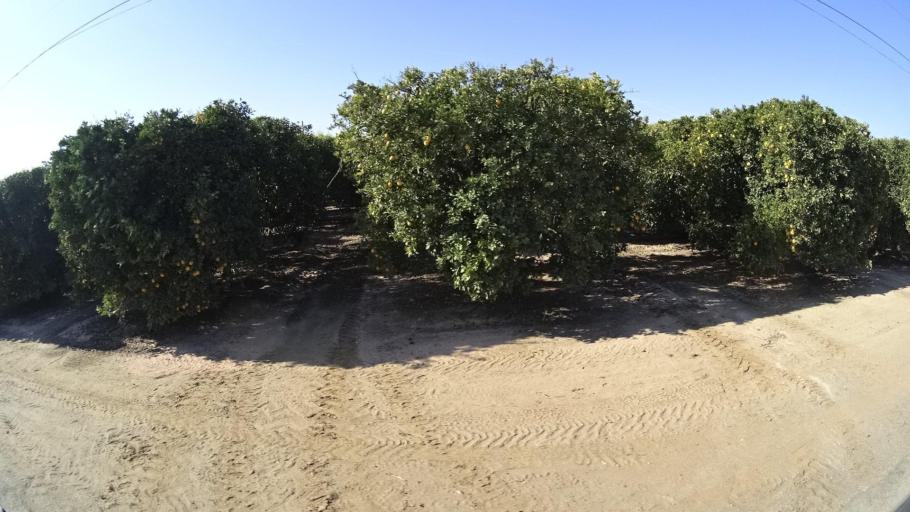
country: US
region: California
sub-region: Tulare County
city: Richgrove
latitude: 35.7194
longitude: -119.1428
